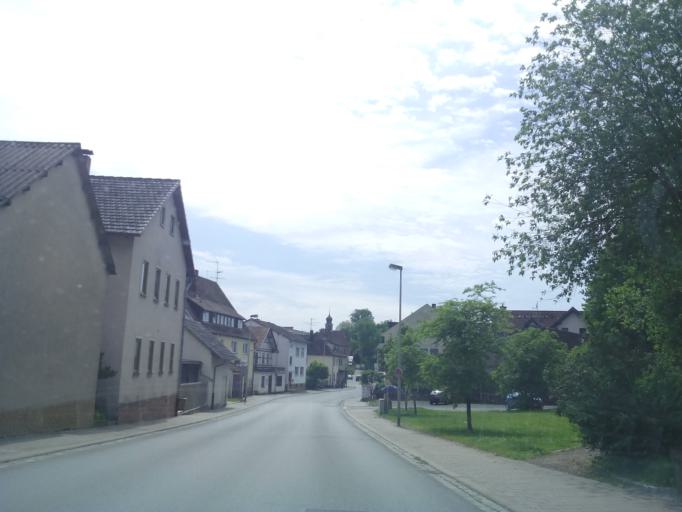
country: DE
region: Bavaria
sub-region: Upper Franconia
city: Weitramsdorf
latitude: 50.2564
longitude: 10.8818
